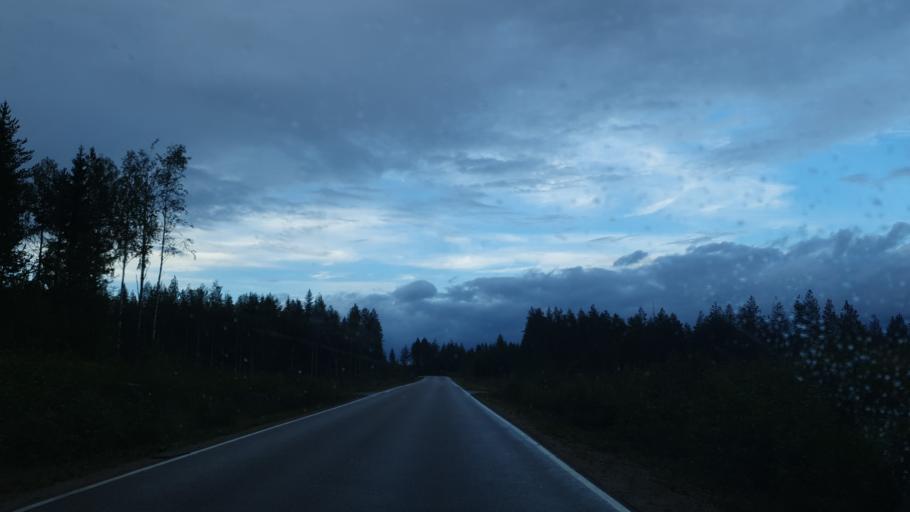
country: FI
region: North Karelia
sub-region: Pielisen Karjala
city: Lieksa
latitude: 63.6253
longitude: 29.8635
